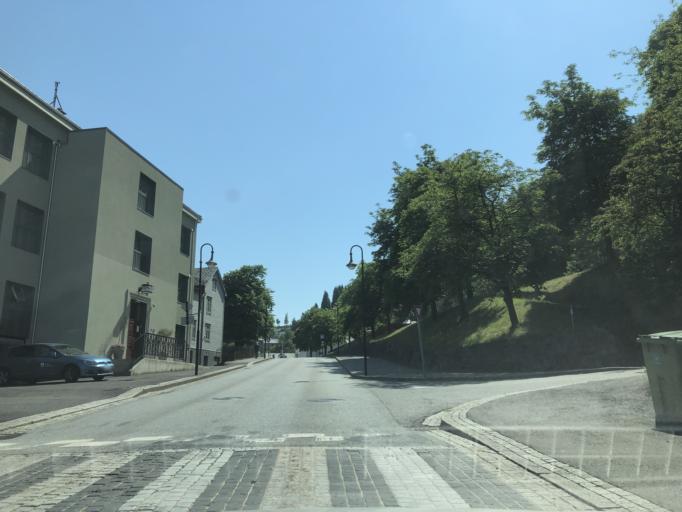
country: NO
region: Hordaland
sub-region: Odda
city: Odda
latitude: 60.0699
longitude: 6.5412
